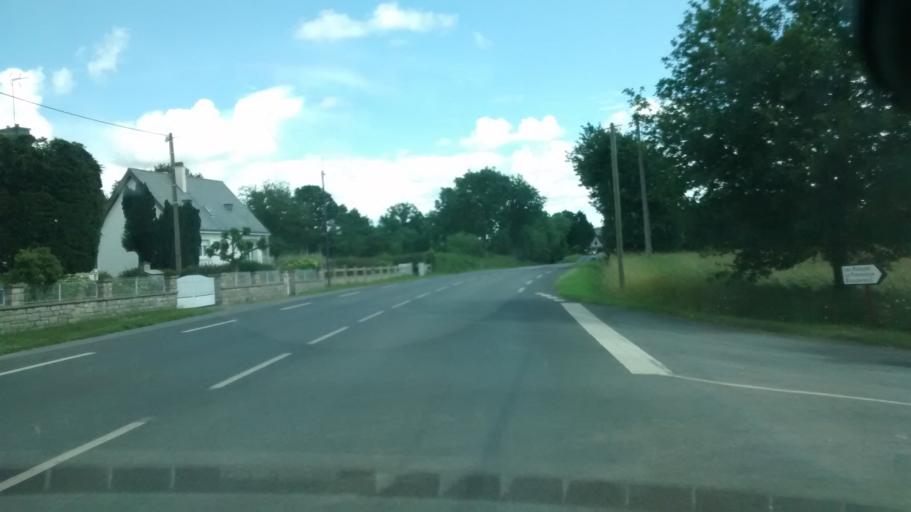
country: FR
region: Brittany
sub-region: Departement du Morbihan
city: Malestroit
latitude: 47.8235
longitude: -2.3787
